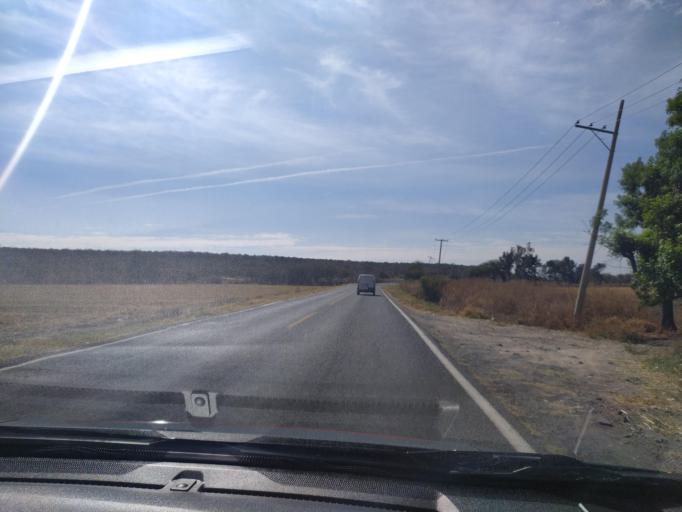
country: MX
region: Guanajuato
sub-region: San Francisco del Rincon
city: San Ignacio de Hidalgo
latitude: 20.9304
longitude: -101.8521
